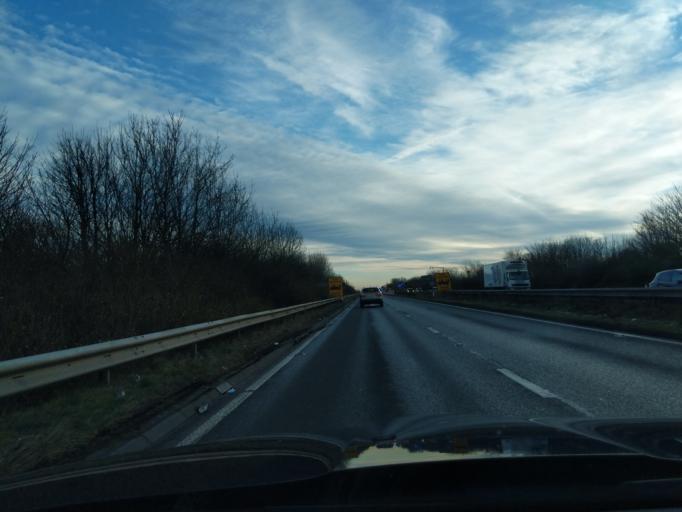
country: GB
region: England
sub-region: Borough of North Tyneside
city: Shiremoor
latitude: 55.0161
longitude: -1.5079
